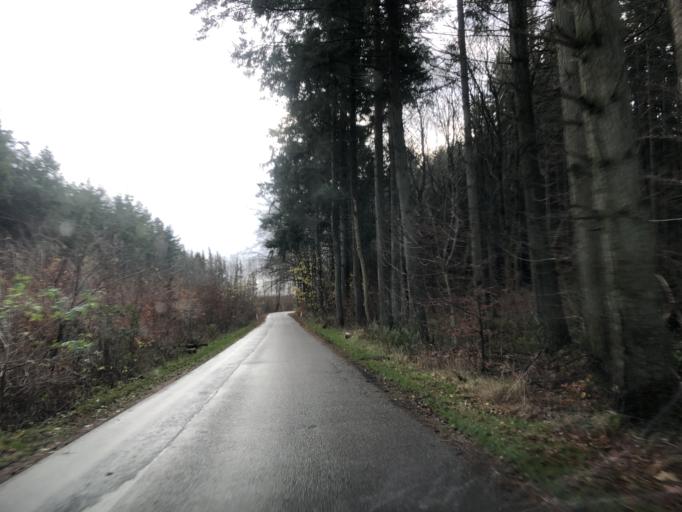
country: DK
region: North Denmark
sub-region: Rebild Kommune
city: Stovring
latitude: 56.9253
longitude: 9.8050
